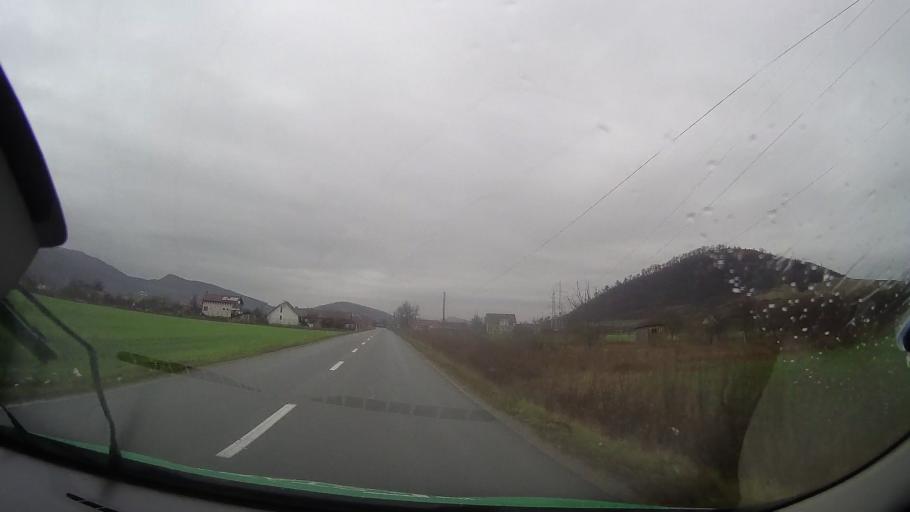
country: RO
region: Bistrita-Nasaud
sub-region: Municipiul Bistrita
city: Viisoara
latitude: 47.0654
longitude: 24.4372
